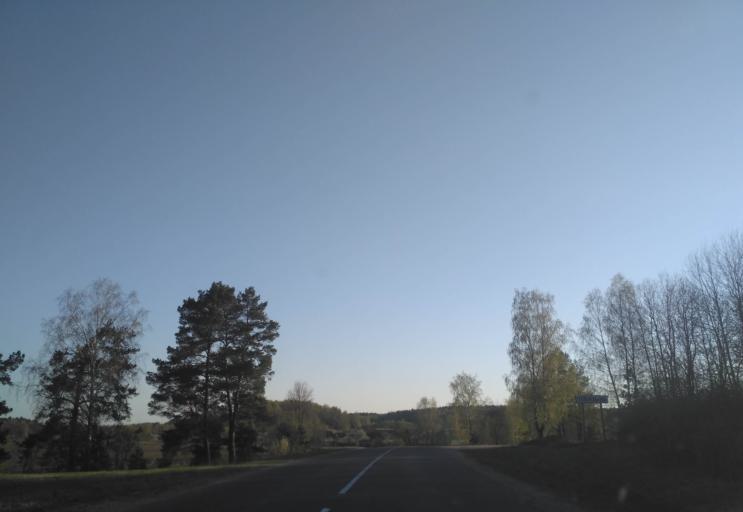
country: BY
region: Minsk
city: Radashkovichy
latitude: 54.1437
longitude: 27.2107
